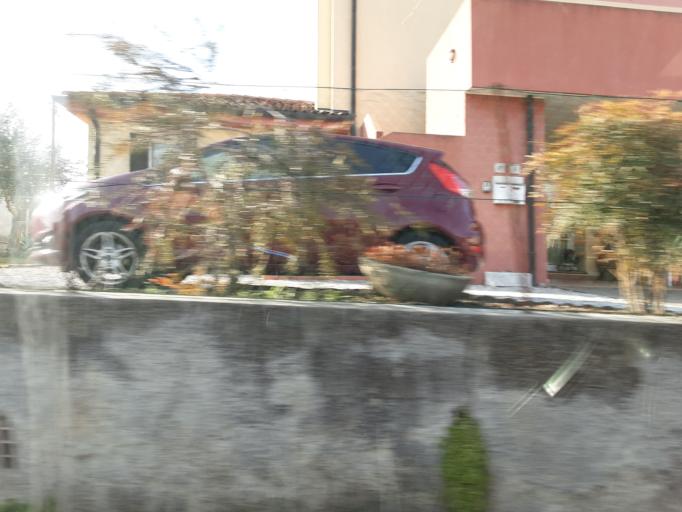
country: IT
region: Veneto
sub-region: Provincia di Treviso
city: Carpesica
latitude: 45.9618
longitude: 12.2846
